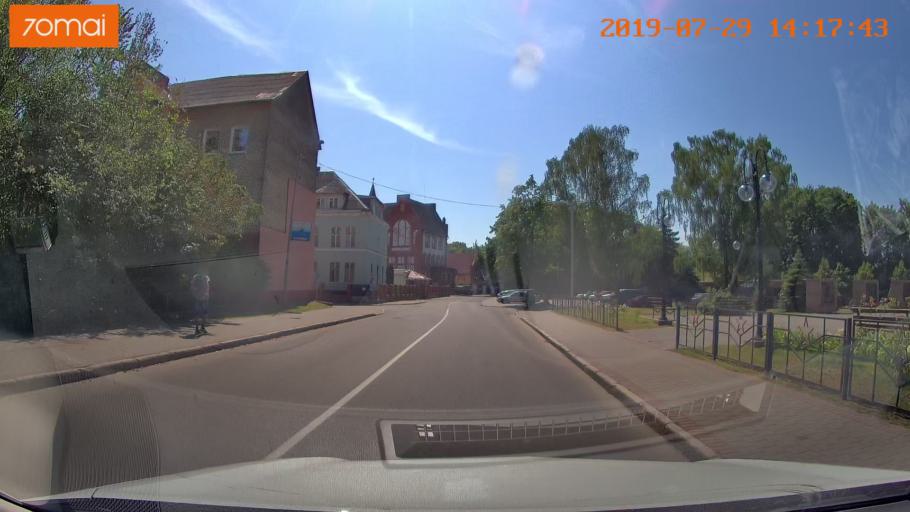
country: RU
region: Kaliningrad
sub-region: Gorod Kaliningrad
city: Baltiysk
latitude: 54.6417
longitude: 19.8908
